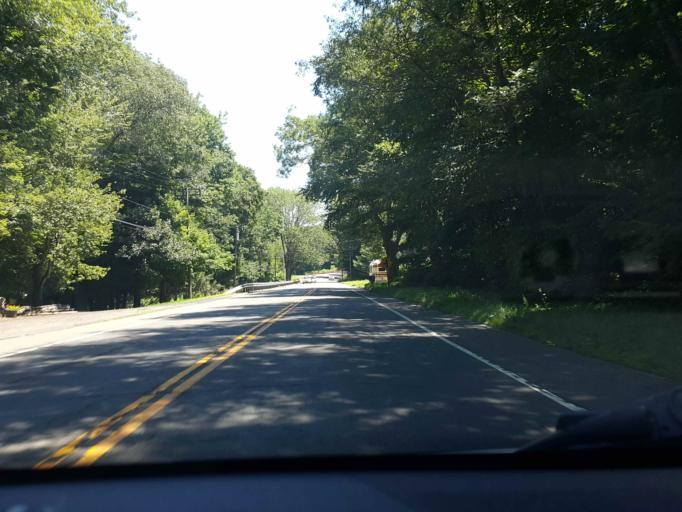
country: US
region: Connecticut
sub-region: New Haven County
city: Guilford
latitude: 41.3064
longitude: -72.7150
